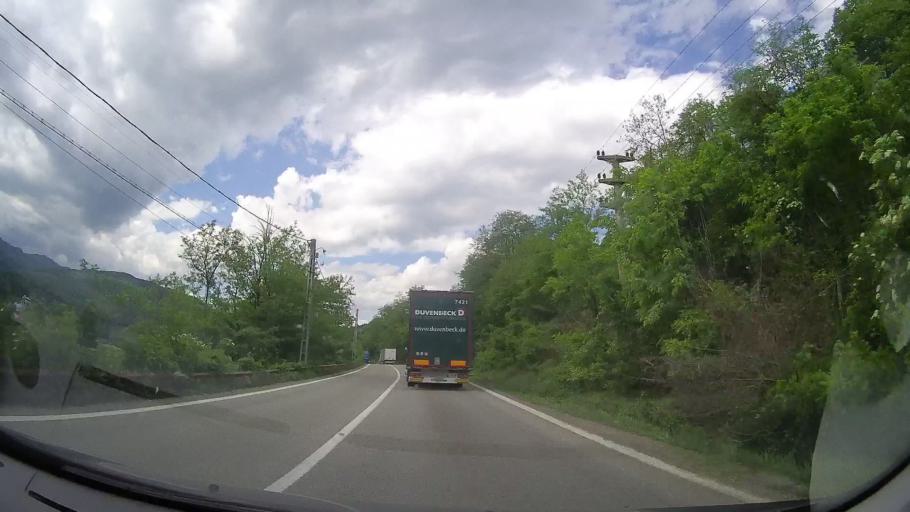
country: RO
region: Valcea
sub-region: Oras Calimanesti
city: Jiblea Veche
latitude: 45.2583
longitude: 24.3355
